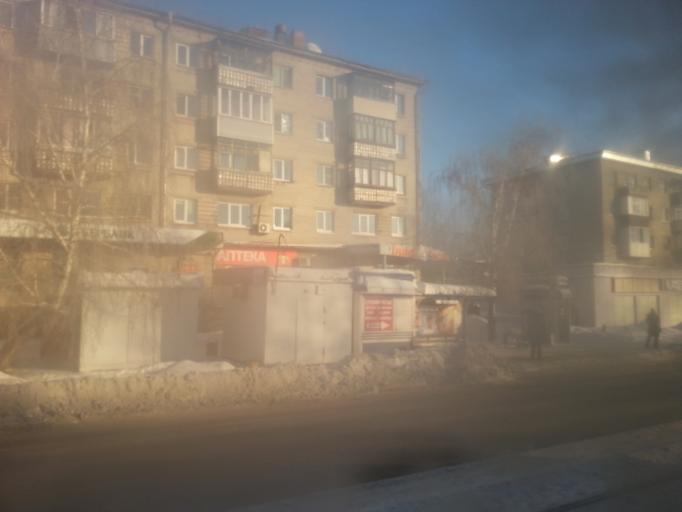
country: RU
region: Altai Krai
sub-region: Gorod Barnaulskiy
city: Barnaul
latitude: 53.3559
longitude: 83.7140
